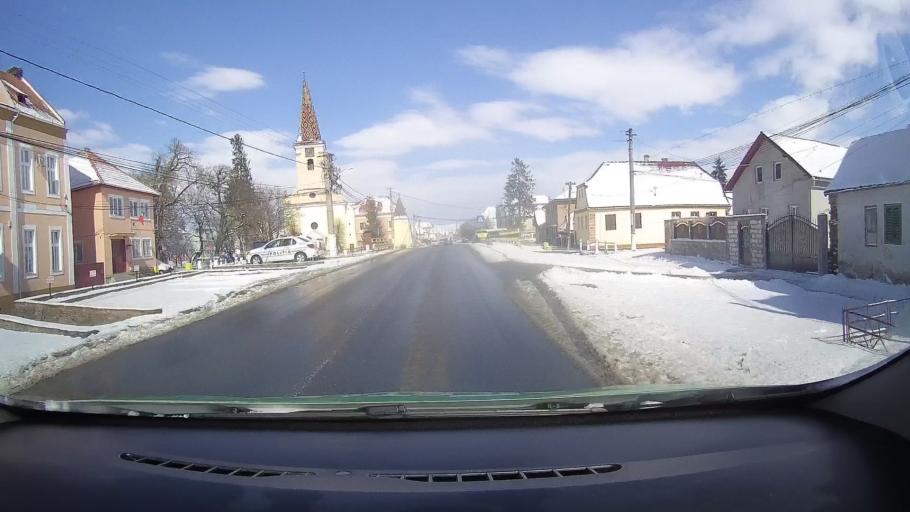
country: RO
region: Sibiu
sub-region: Comuna Nocrich
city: Nocrich
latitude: 45.8946
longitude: 24.4546
